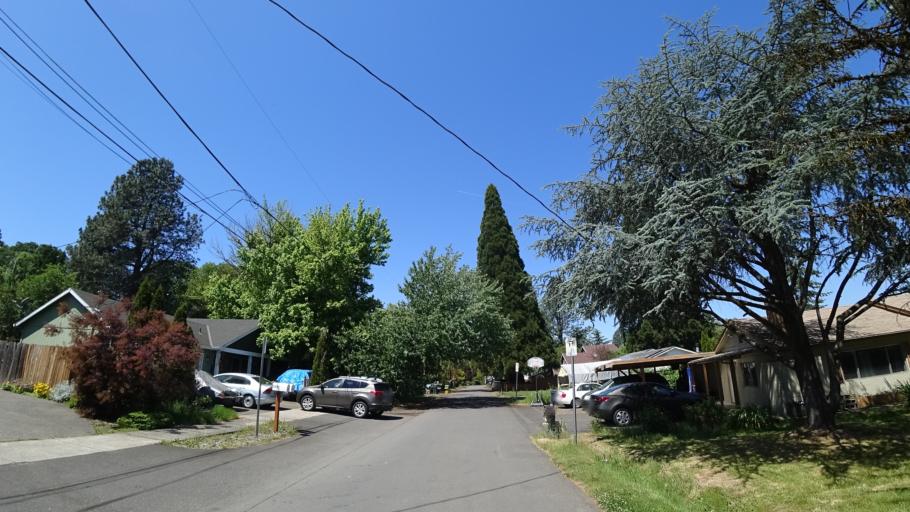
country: US
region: Oregon
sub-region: Washington County
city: Aloha
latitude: 45.4958
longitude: -122.8527
